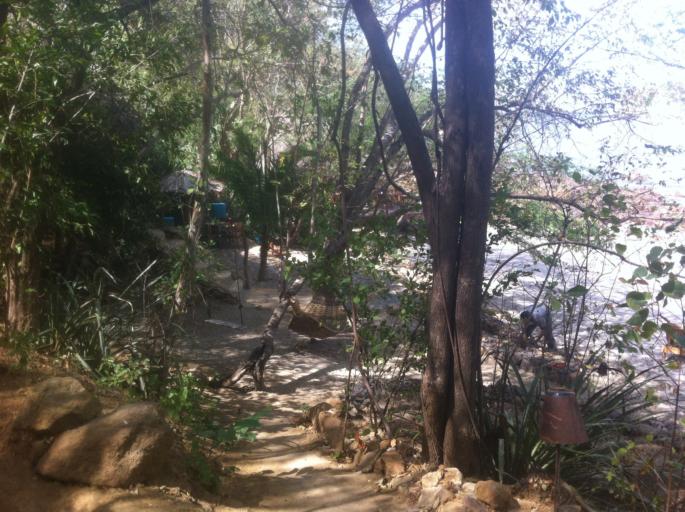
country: NI
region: Rivas
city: Tola
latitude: 11.3811
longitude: -86.0301
